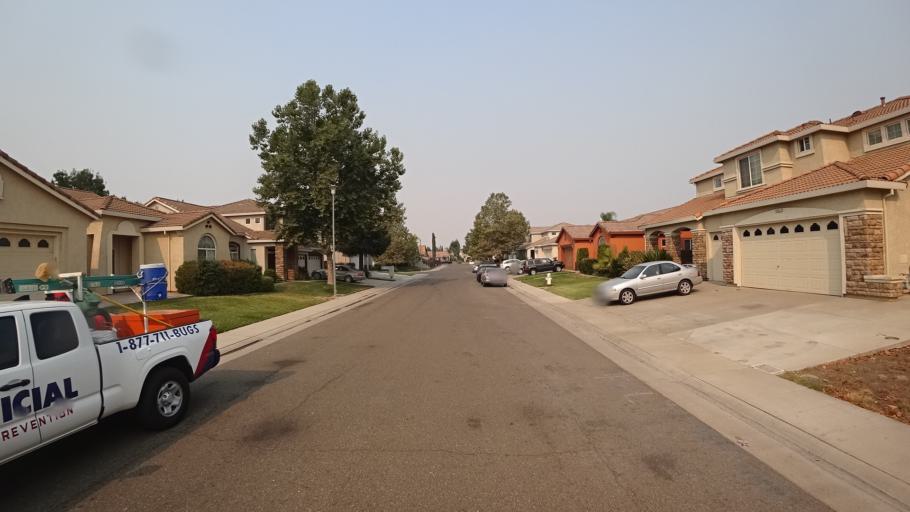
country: US
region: California
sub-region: Sacramento County
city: Laguna
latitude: 38.3958
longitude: -121.4304
